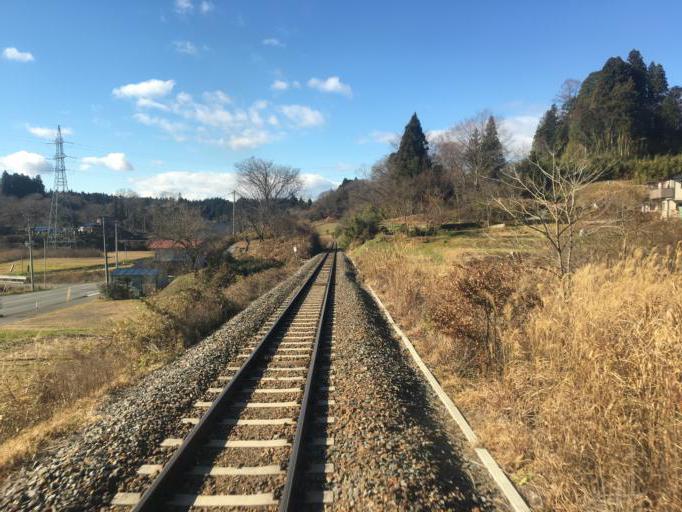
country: JP
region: Iwate
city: Ichinoseki
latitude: 38.9306
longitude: 141.3711
